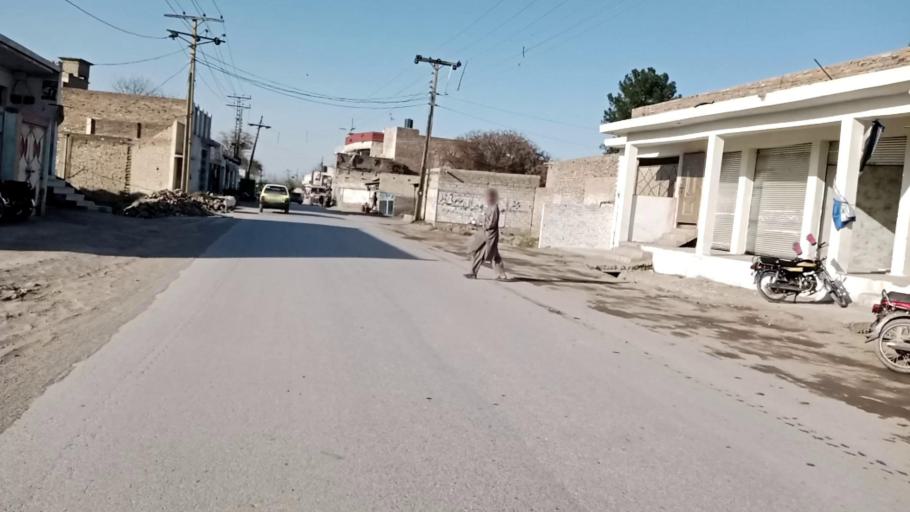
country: PK
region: Khyber Pakhtunkhwa
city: Peshawar
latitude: 34.0751
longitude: 71.5336
